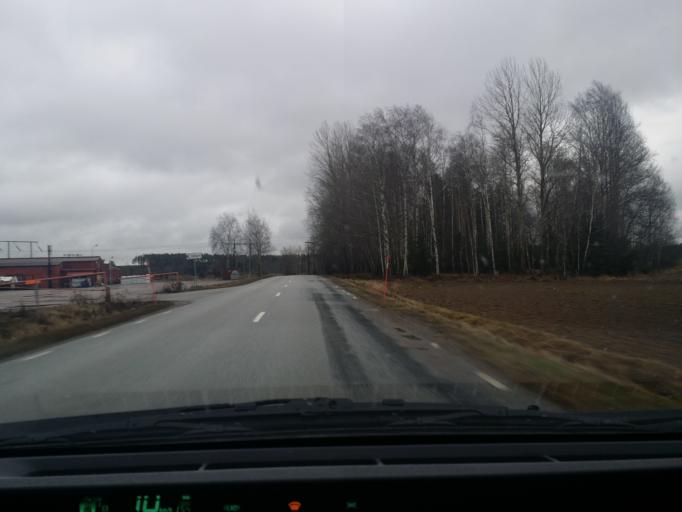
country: SE
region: Vaestmanland
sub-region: Sala Kommun
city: Sala
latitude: 59.8071
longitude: 16.5273
